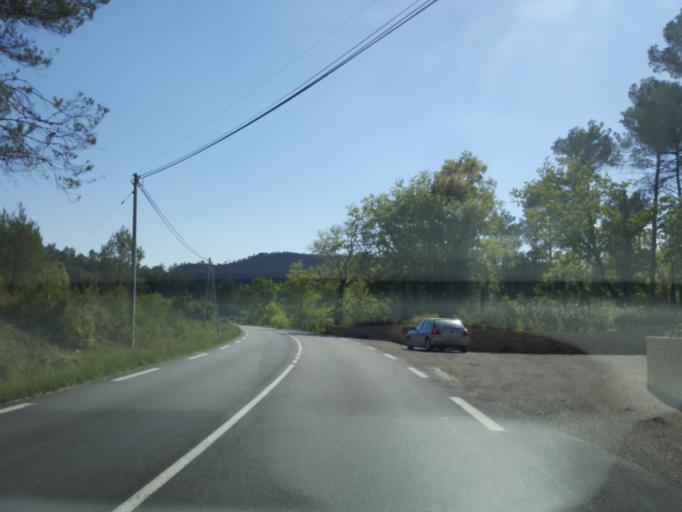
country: FR
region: Provence-Alpes-Cote d'Azur
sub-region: Departement du Var
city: La Roquebrussanne
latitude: 43.3594
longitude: 5.9731
